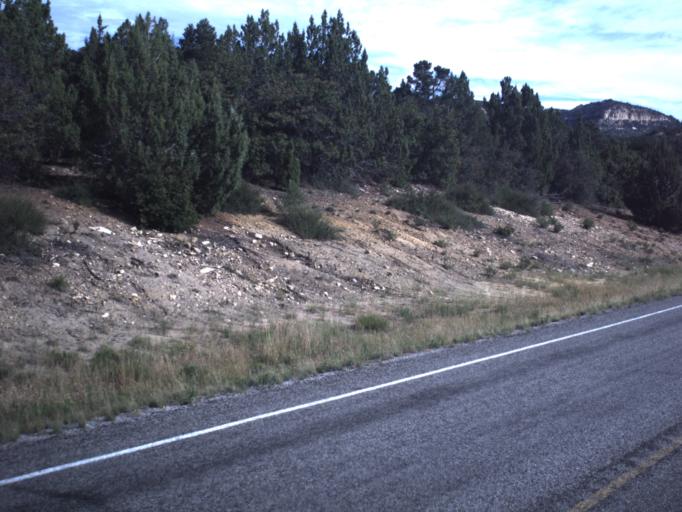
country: US
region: Utah
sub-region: Washington County
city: Hildale
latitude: 37.2567
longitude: -112.7924
